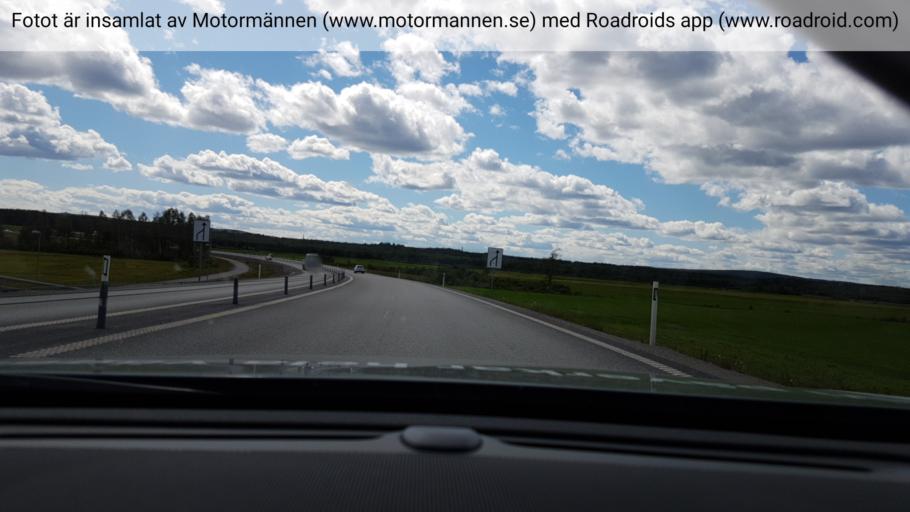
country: SE
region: Vaesterbotten
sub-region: Umea Kommun
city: Roback
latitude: 63.8558
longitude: 20.1979
